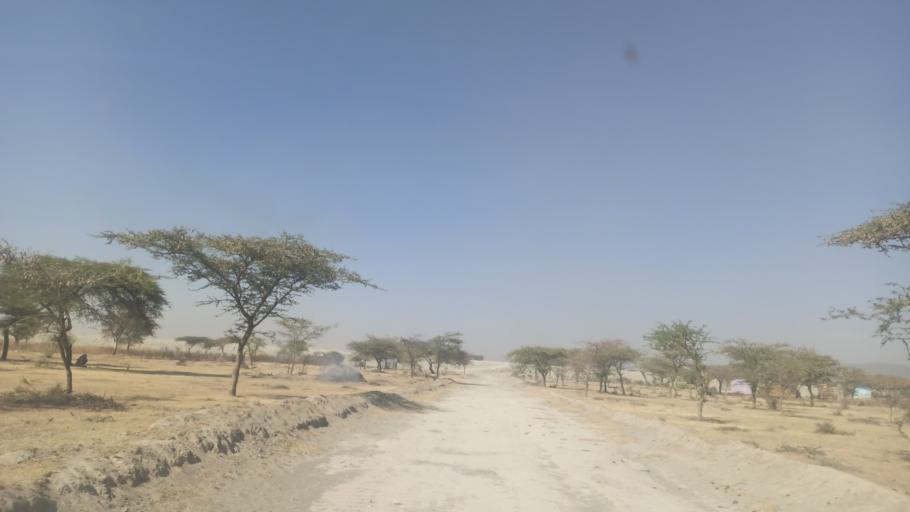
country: ET
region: Oromiya
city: Ziway
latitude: 7.6897
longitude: 38.6561
